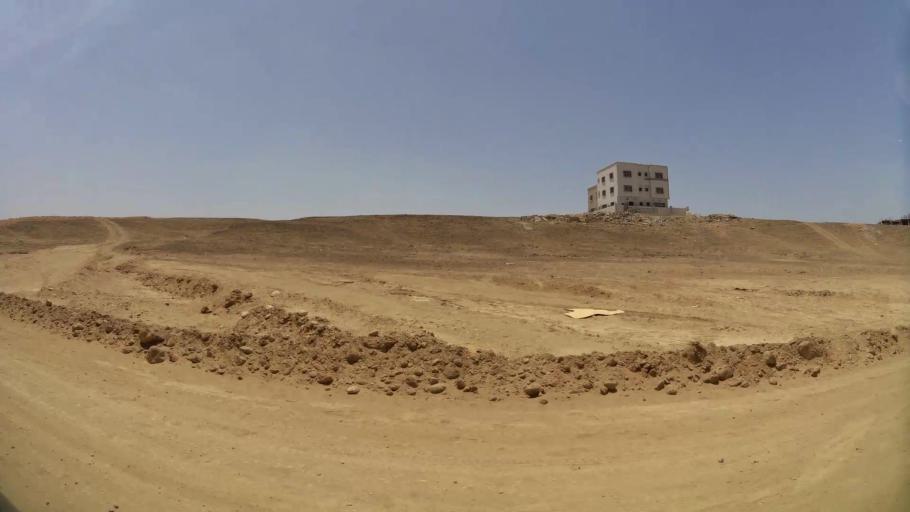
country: OM
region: Zufar
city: Salalah
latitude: 17.0787
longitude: 54.1859
